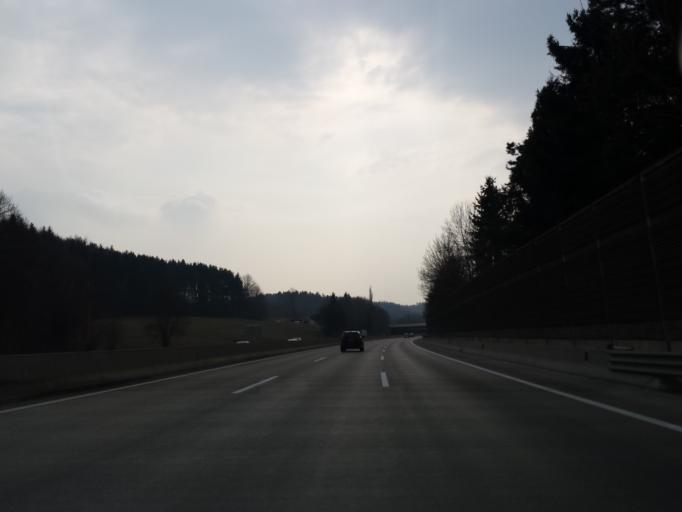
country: AT
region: Styria
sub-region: Politischer Bezirk Weiz
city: Ungerdorf
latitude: 47.0944
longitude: 15.6814
